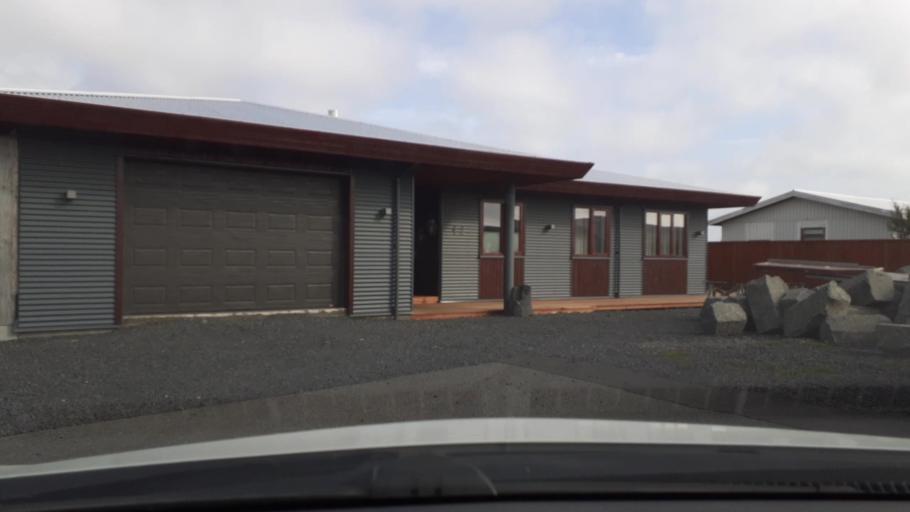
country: IS
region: South
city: THorlakshoefn
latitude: 63.8579
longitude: -21.3969
